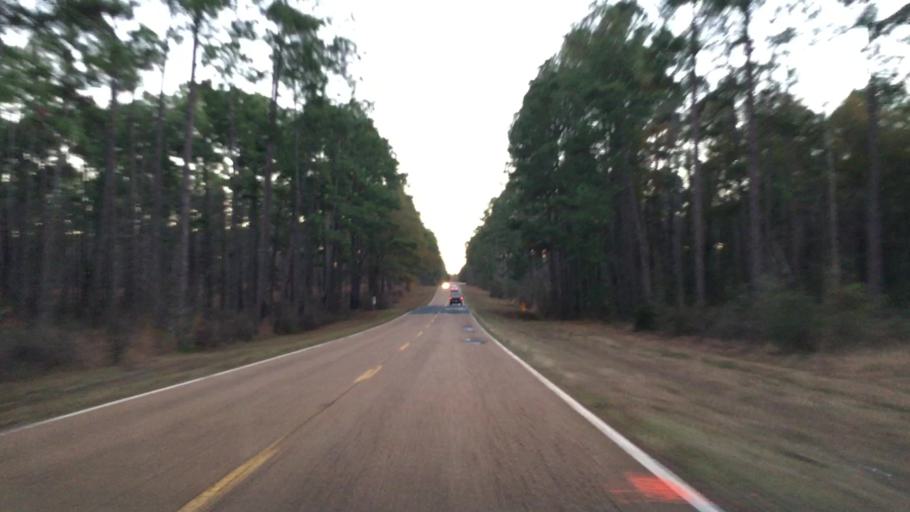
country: US
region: Louisiana
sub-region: Vernon Parish
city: Fort Polk South
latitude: 31.0103
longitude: -93.1859
